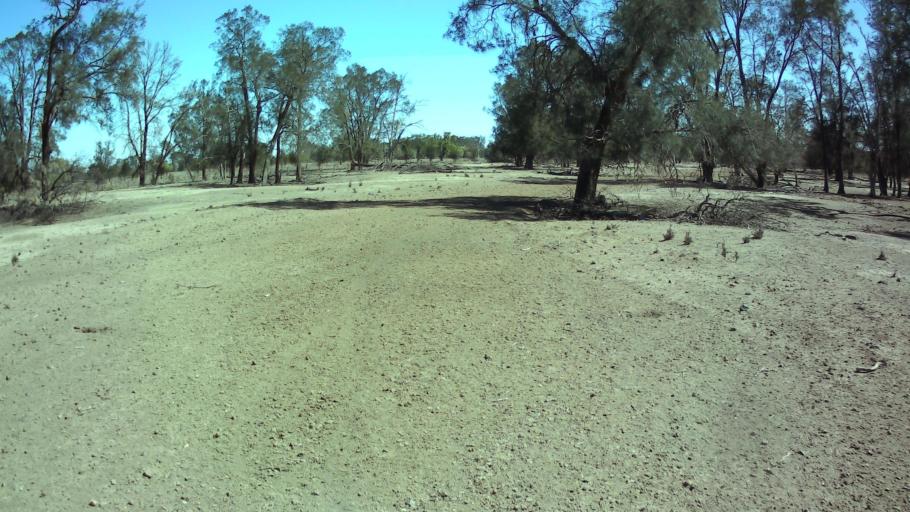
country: AU
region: New South Wales
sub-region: Bland
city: West Wyalong
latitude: -33.7615
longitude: 147.6585
